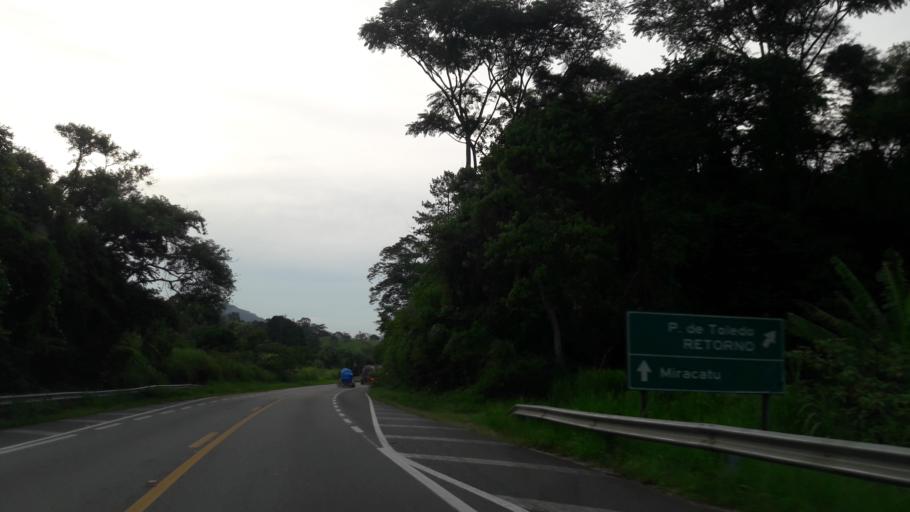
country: BR
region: Sao Paulo
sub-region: Miracatu
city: Miracatu
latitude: -24.2809
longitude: -47.2369
